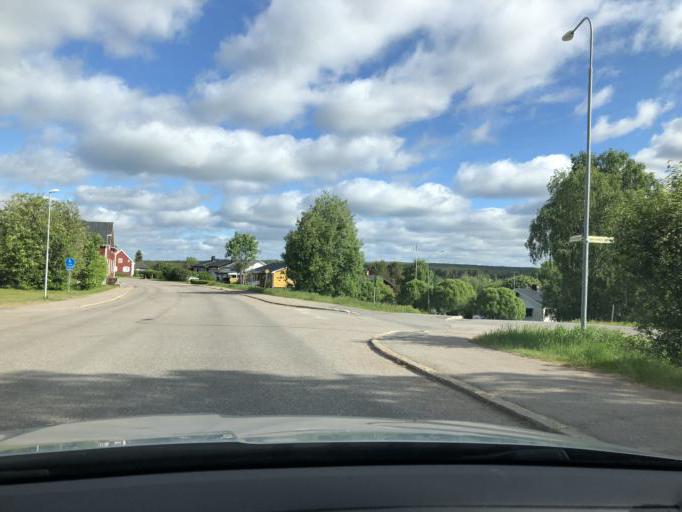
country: SE
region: Norrbotten
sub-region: Pajala Kommun
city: Pajala
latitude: 67.2143
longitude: 23.3667
